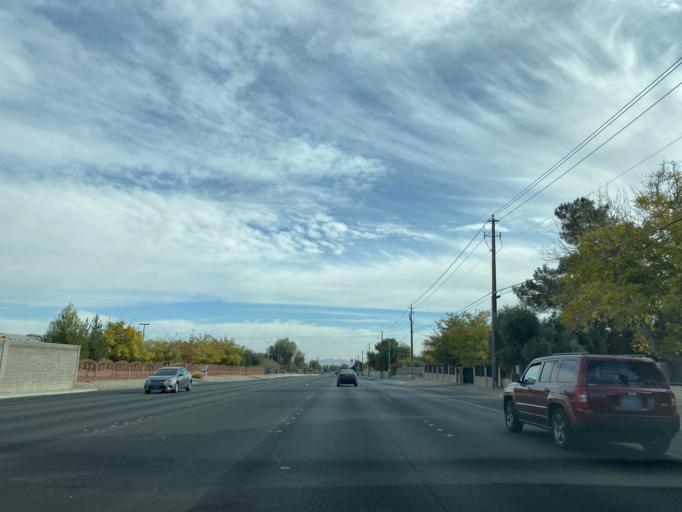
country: US
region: Nevada
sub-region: Clark County
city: Las Vegas
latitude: 36.2469
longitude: -115.2313
